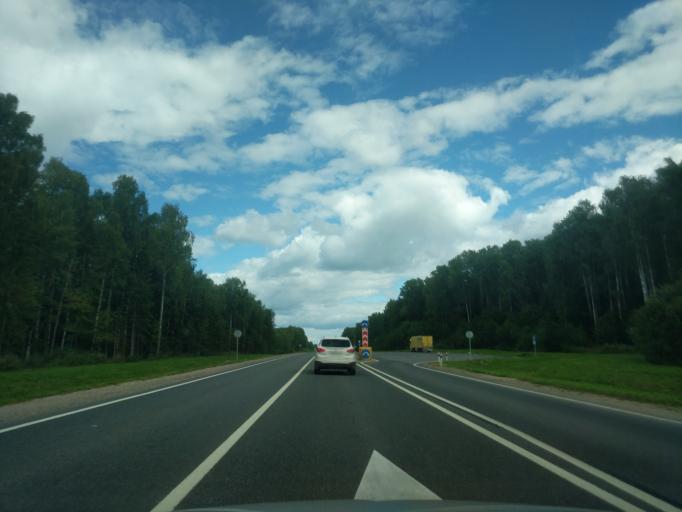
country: RU
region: Kostroma
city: Oktyabr'skiy
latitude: 57.7912
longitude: 41.1564
